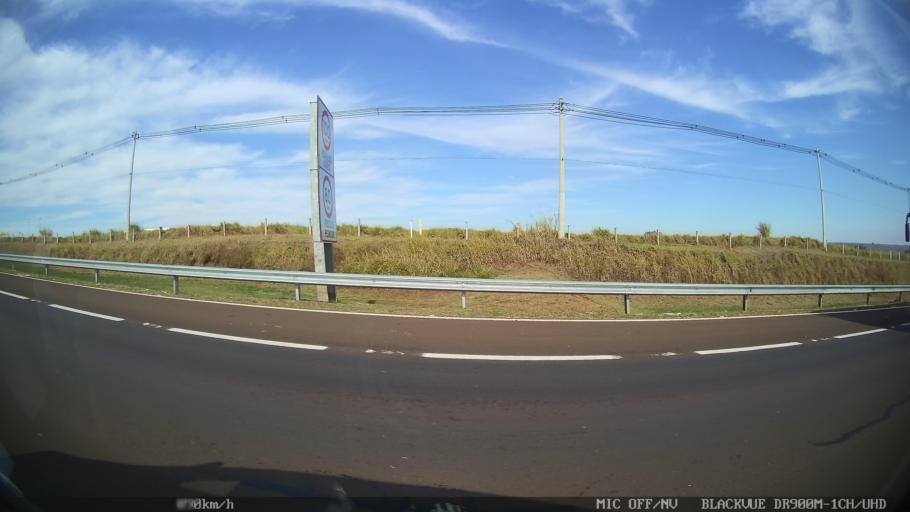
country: BR
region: Sao Paulo
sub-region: Americo Brasiliense
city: Americo Brasiliense
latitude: -21.7782
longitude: -48.1060
